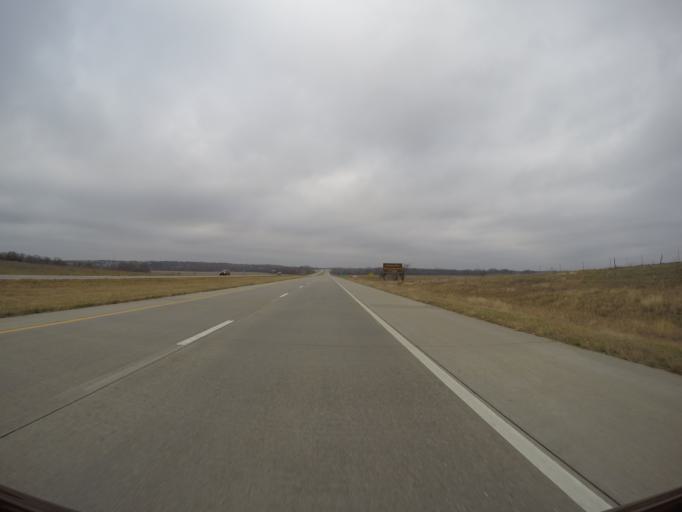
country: US
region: Kansas
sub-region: Dickinson County
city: Chapman
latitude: 38.9900
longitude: -97.0079
